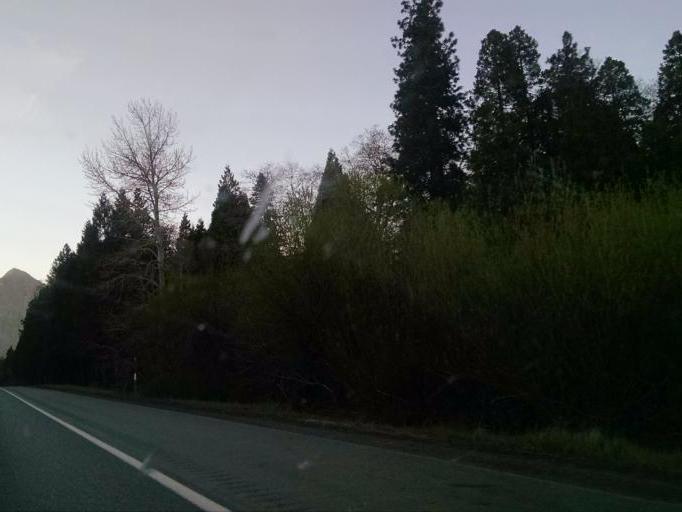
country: US
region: California
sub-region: Siskiyou County
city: Mount Shasta
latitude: 41.3202
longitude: -122.3255
